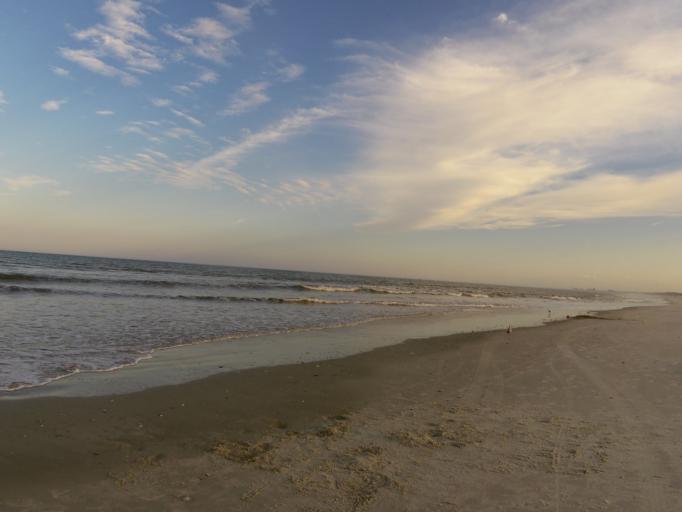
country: US
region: Florida
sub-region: Duval County
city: Atlantic Beach
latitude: 30.3815
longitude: -81.3966
